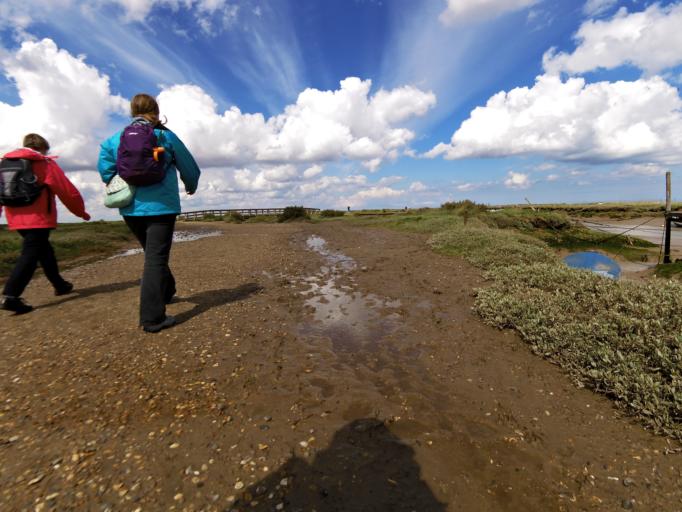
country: GB
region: England
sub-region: Norfolk
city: Briston
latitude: 52.9591
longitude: 0.9839
